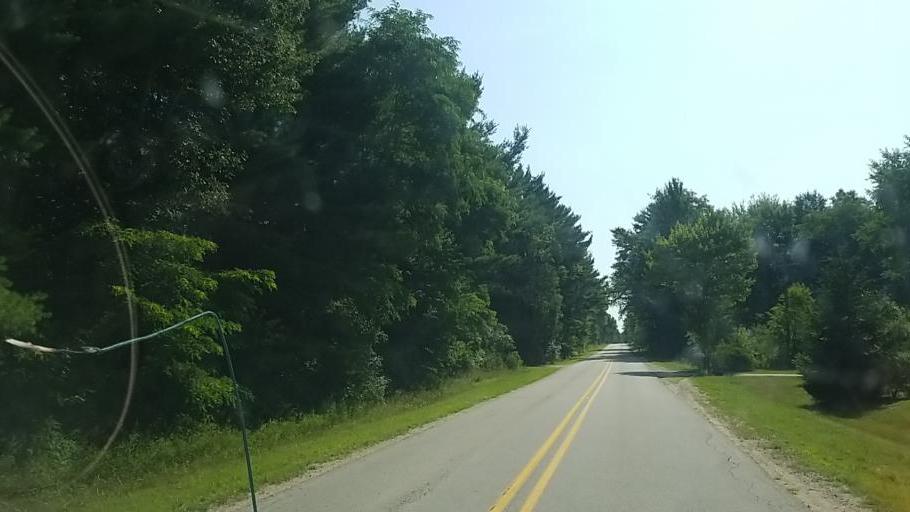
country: US
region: Michigan
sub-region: Muskegon County
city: Whitehall
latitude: 43.3704
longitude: -86.3557
